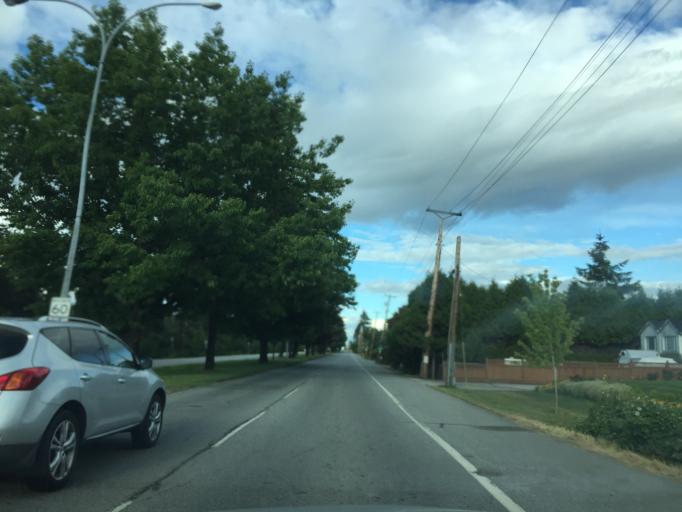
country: CA
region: British Columbia
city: Richmond
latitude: 49.1700
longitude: -123.1028
